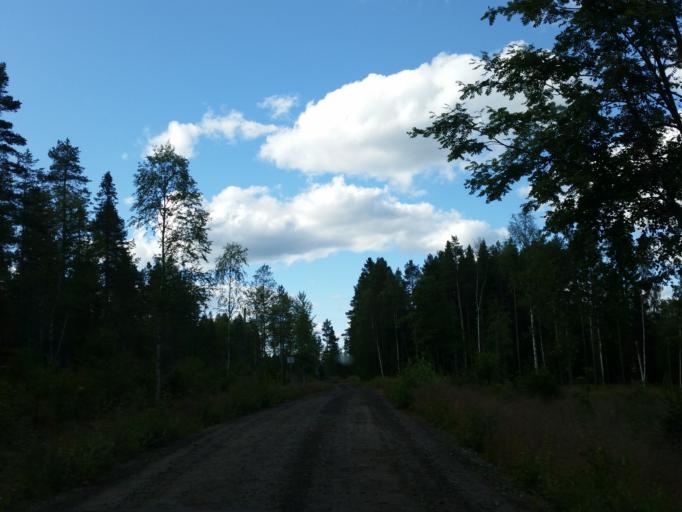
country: SE
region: Vaesterbotten
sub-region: Robertsfors Kommun
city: Robertsfors
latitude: 64.1342
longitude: 20.9427
